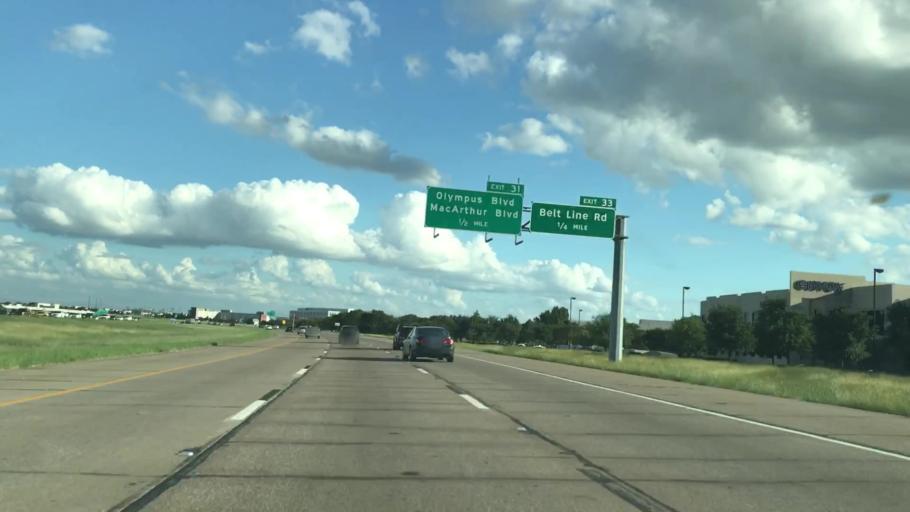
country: US
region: Texas
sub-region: Dallas County
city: Coppell
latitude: 32.9289
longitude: -97.0035
